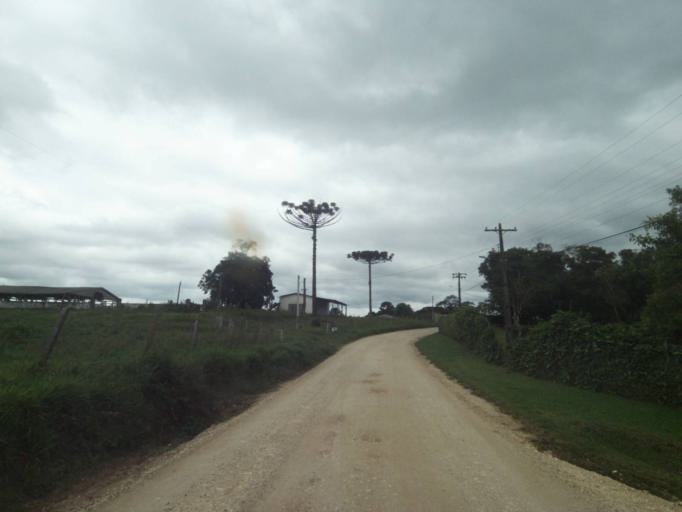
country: BR
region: Parana
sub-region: Campina Grande Do Sul
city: Campina Grande do Sul
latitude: -25.3256
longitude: -49.0885
